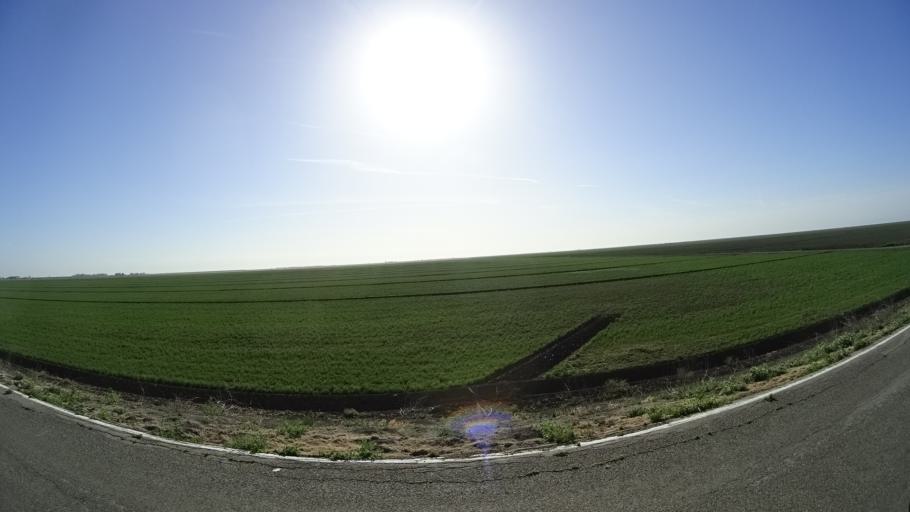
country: US
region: California
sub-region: Kings County
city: Stratford
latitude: 36.1391
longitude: -119.7982
